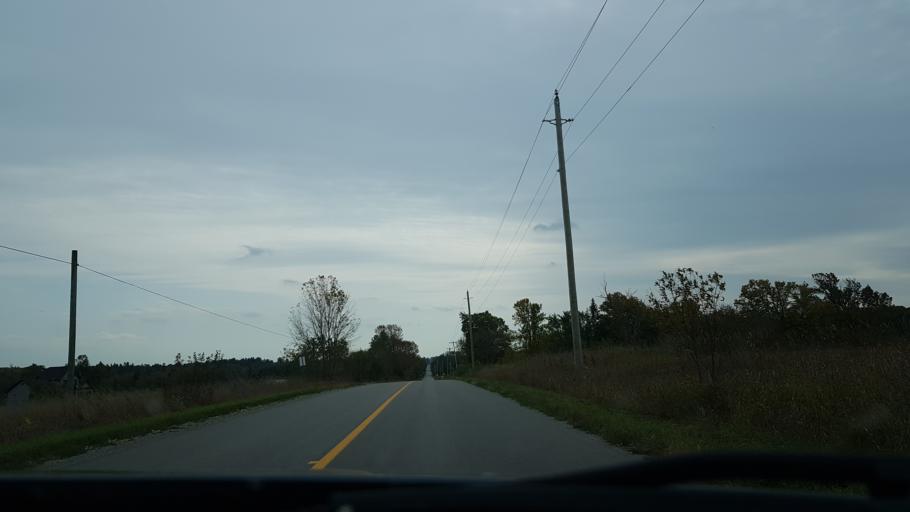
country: CA
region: Ontario
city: Orillia
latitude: 44.6250
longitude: -78.9531
